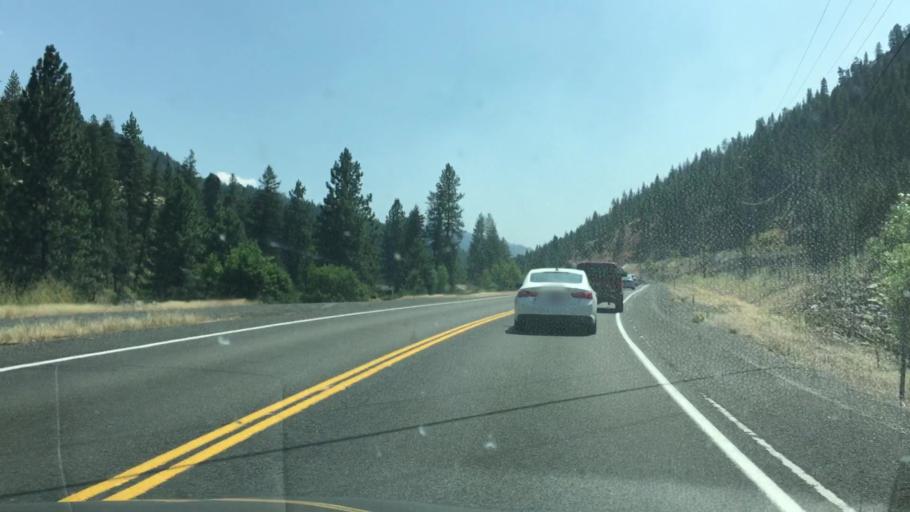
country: US
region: Idaho
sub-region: Valley County
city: McCall
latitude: 45.2202
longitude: -116.3184
